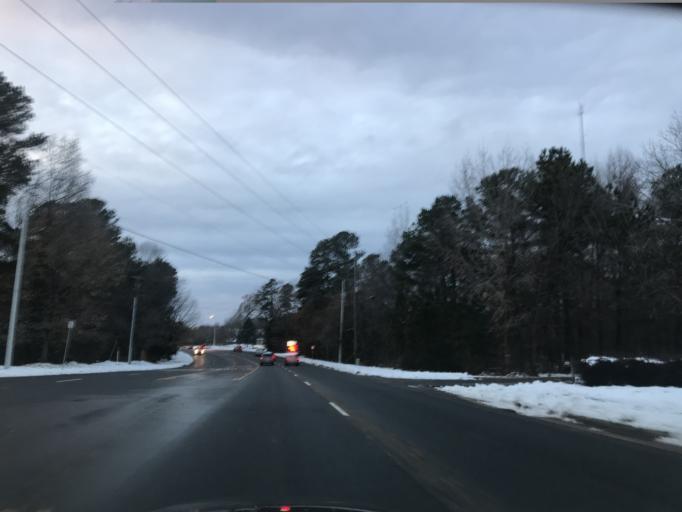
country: US
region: North Carolina
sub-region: Wake County
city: Wake Forest
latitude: 35.9022
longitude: -78.5812
